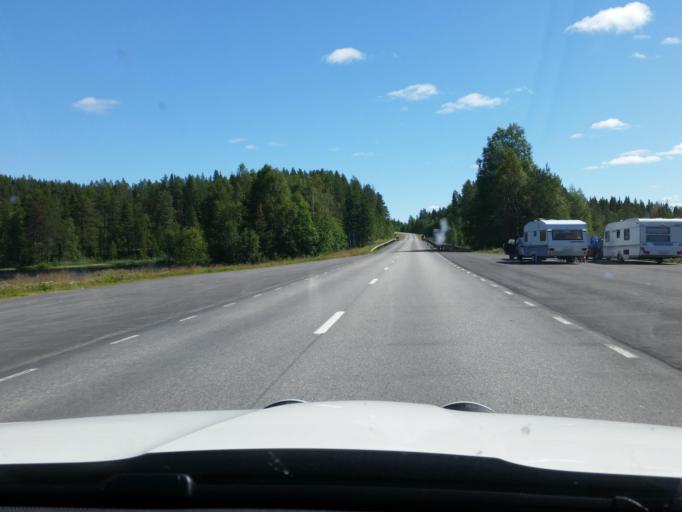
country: SE
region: Vaesterbotten
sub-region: Skelleftea Kommun
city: Storvik
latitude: 65.3291
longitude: 20.6107
